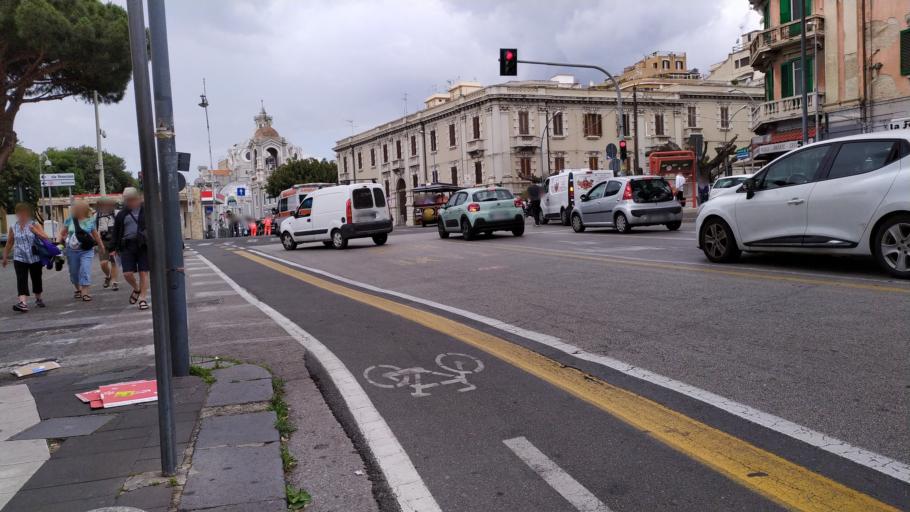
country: IT
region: Sicily
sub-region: Messina
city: Messina
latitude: 38.1897
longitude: 15.5518
